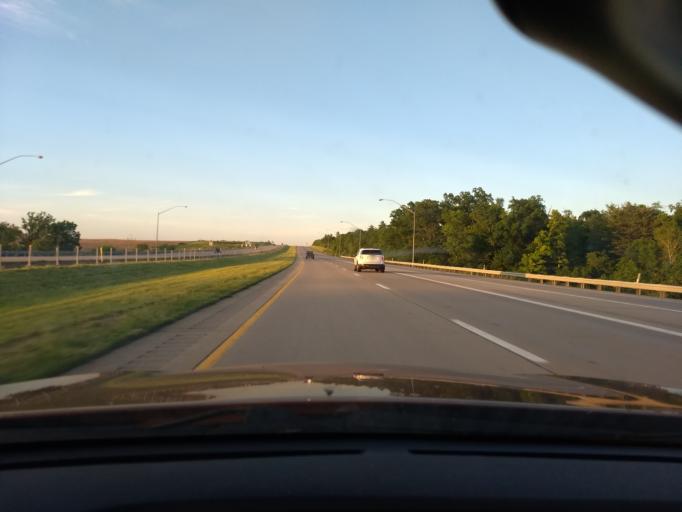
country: US
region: Pennsylvania
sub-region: Centre County
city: Houserville
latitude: 40.8486
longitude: -77.8072
